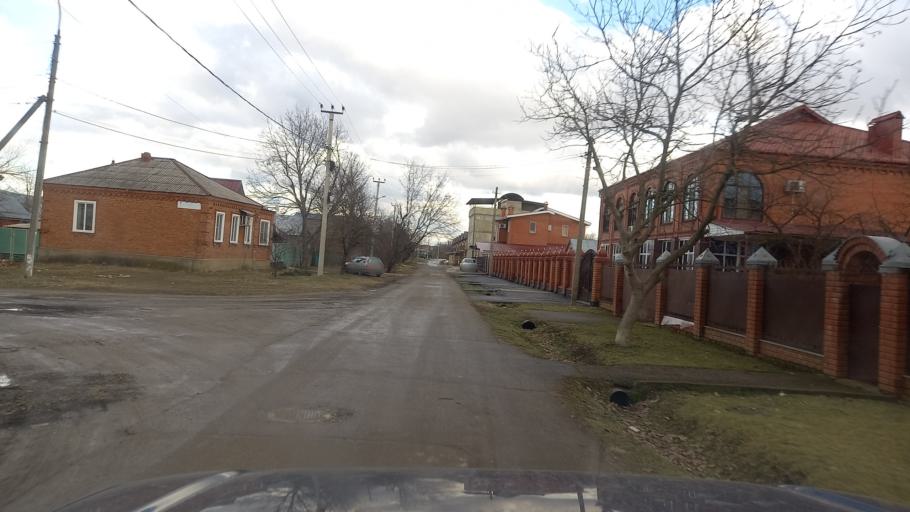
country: RU
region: Adygeya
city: Maykop
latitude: 44.5963
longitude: 40.0692
